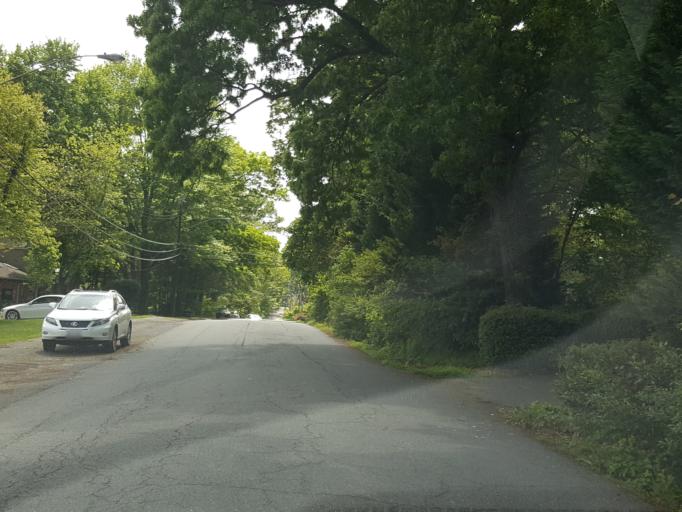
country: US
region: Virginia
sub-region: Fairfax County
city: Annandale
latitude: 38.8476
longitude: -77.2063
